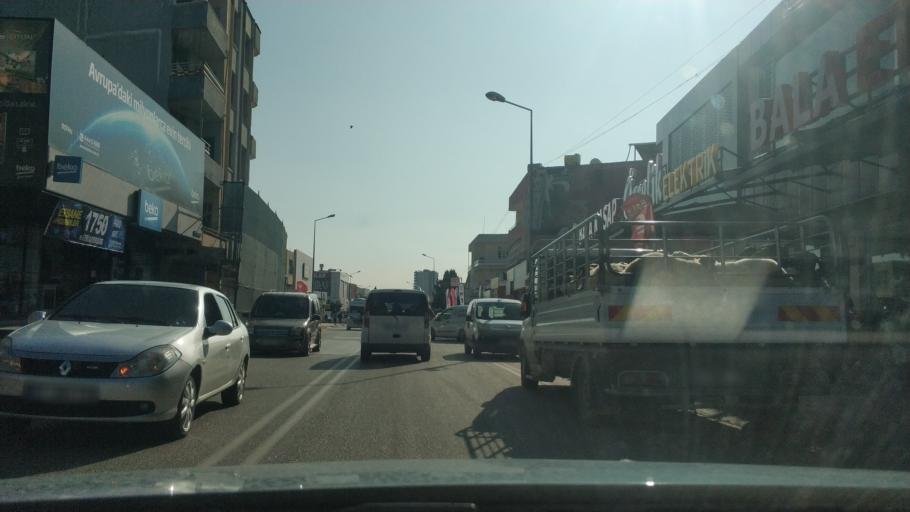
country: TR
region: Adana
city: Seyhan
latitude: 37.0166
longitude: 35.3000
